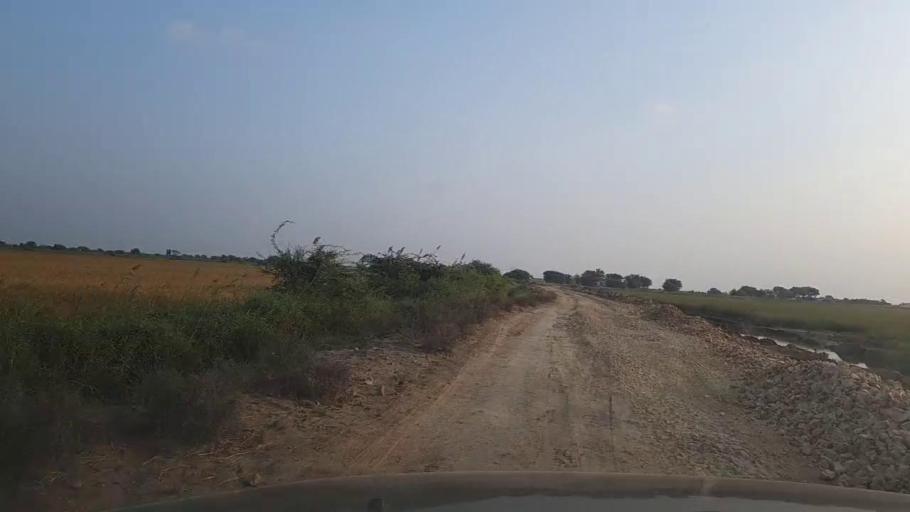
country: PK
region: Sindh
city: Jati
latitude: 24.5396
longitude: 68.3601
